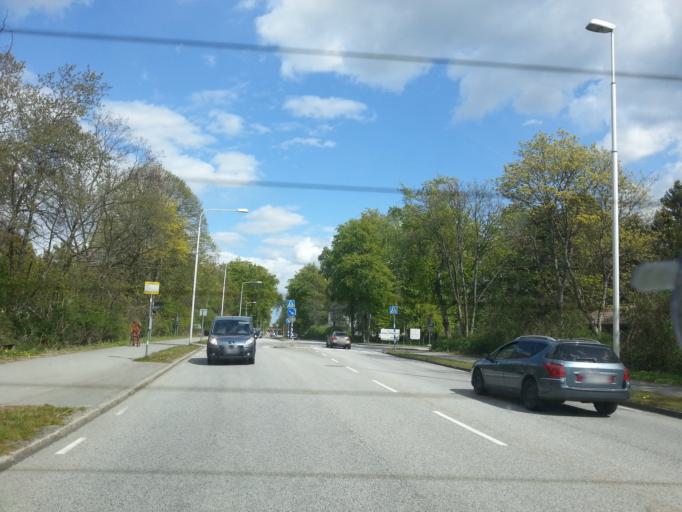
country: SE
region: Skane
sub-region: Ystads Kommun
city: Ystad
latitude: 55.4304
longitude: 13.8469
